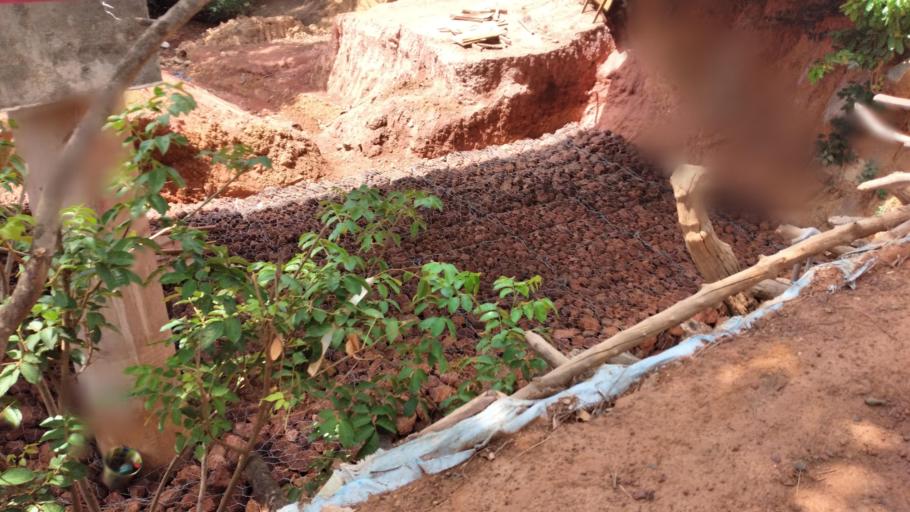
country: ML
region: Koulikoro
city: Kangaba
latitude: 12.0724
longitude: -8.5370
